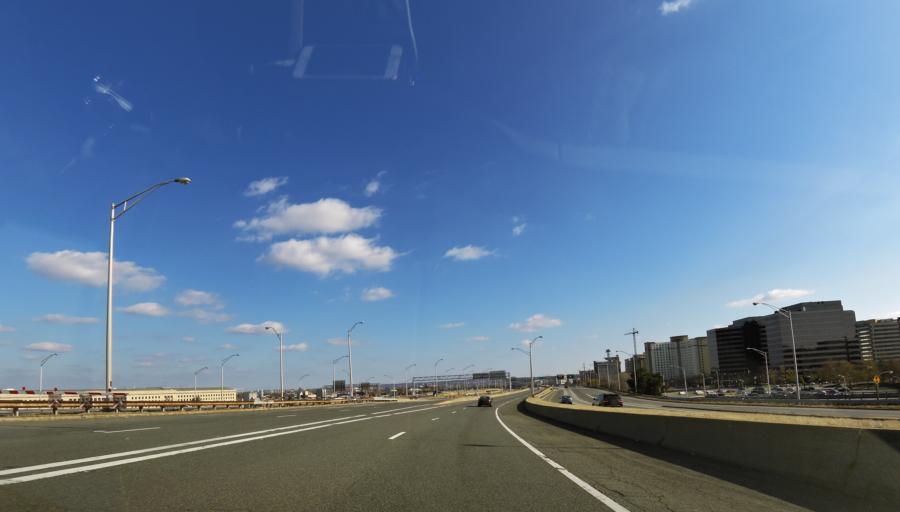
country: US
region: Washington, D.C.
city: Washington, D.C.
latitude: 38.8672
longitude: -77.0615
